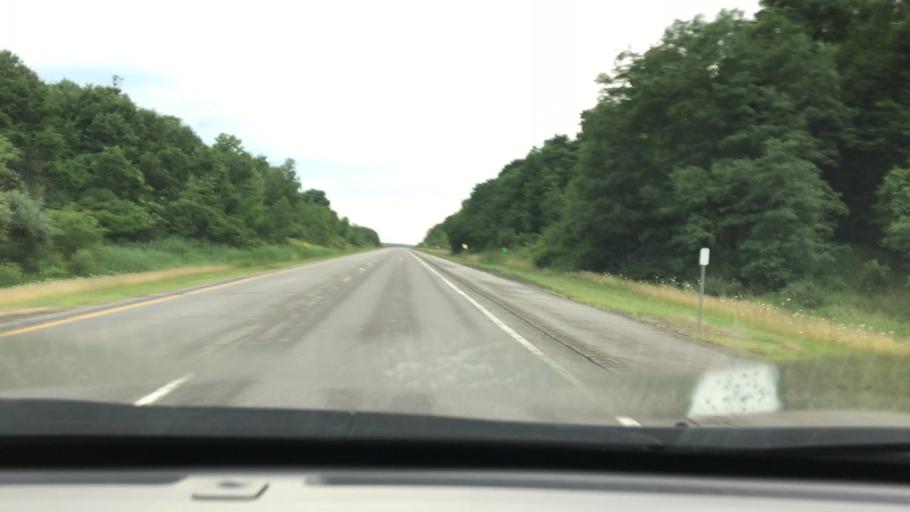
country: US
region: New York
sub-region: Erie County
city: Springville
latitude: 42.5800
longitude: -78.7237
